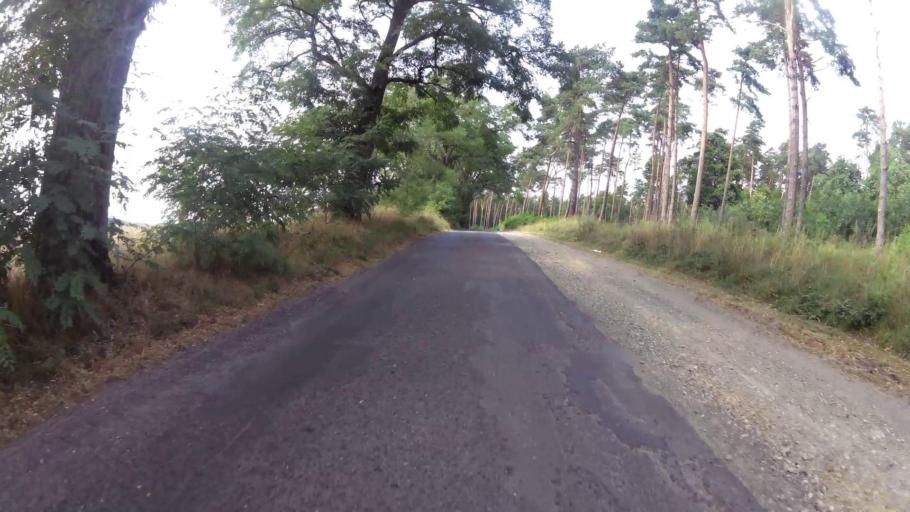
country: PL
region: West Pomeranian Voivodeship
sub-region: Powiat gryfinski
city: Mieszkowice
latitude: 52.8713
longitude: 14.5195
